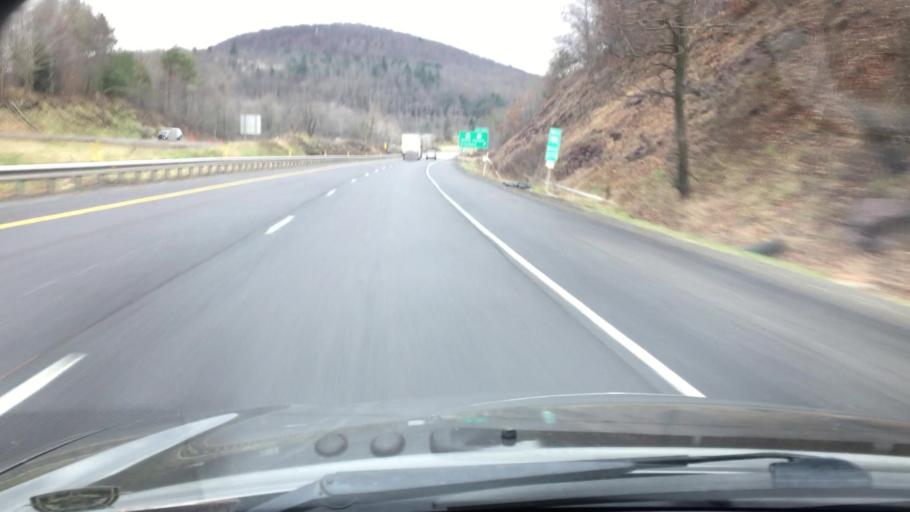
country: US
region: Pennsylvania
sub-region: Luzerne County
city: White Haven
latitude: 41.0564
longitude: -75.7669
